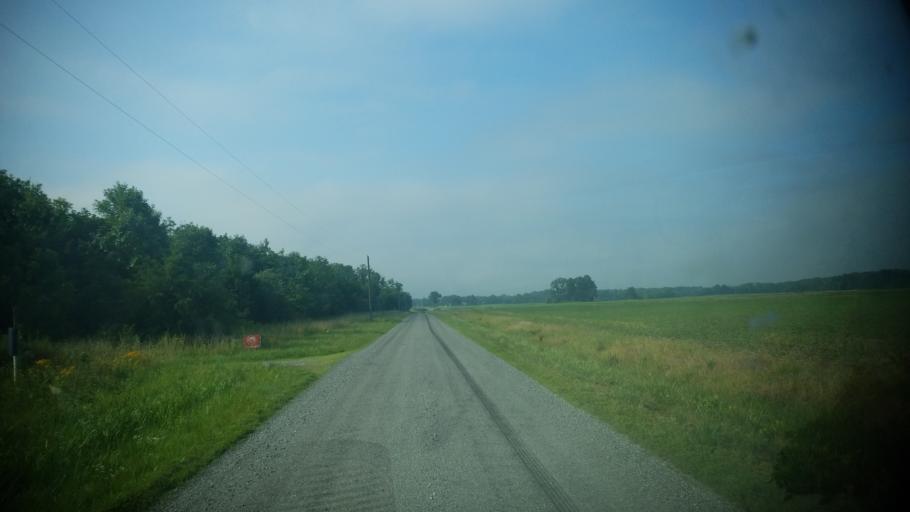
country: US
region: Illinois
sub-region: Clay County
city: Flora
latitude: 38.5940
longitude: -88.3644
